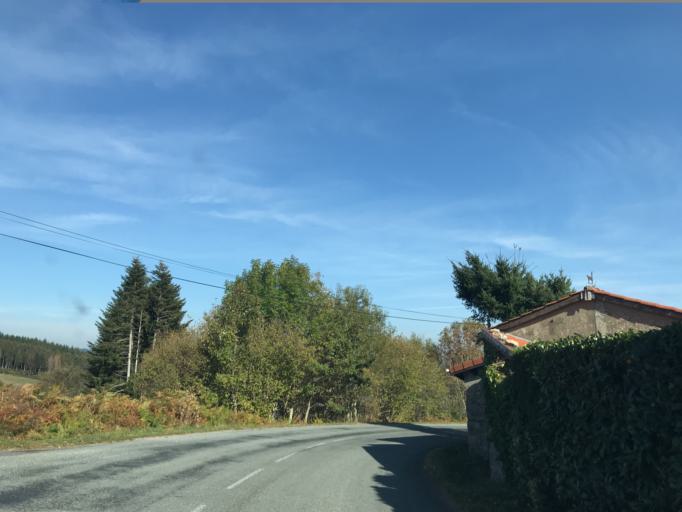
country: FR
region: Rhone-Alpes
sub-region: Departement de la Loire
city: Noiretable
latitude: 45.8100
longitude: 3.7381
